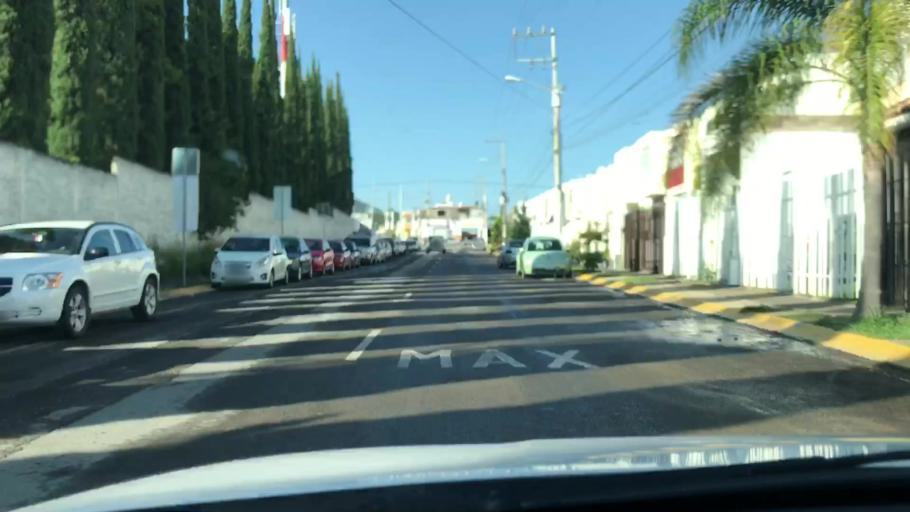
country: MX
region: Jalisco
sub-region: Tlajomulco de Zuniga
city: Palomar
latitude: 20.6276
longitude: -103.4781
